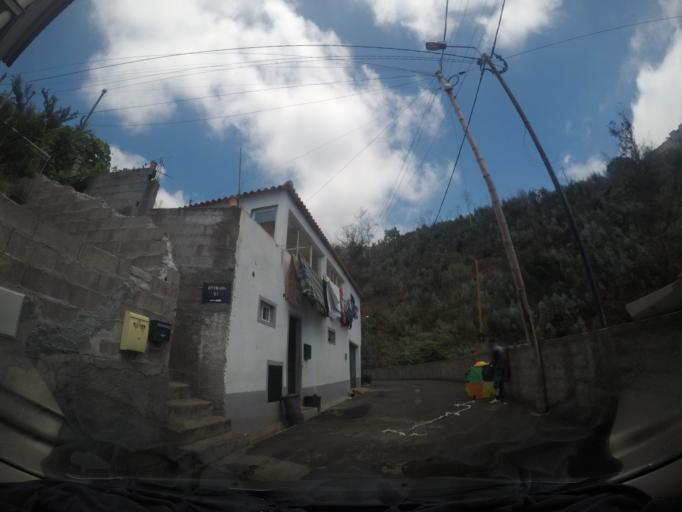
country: PT
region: Madeira
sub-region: Funchal
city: Nossa Senhora do Monte
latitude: 32.6766
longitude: -16.9234
